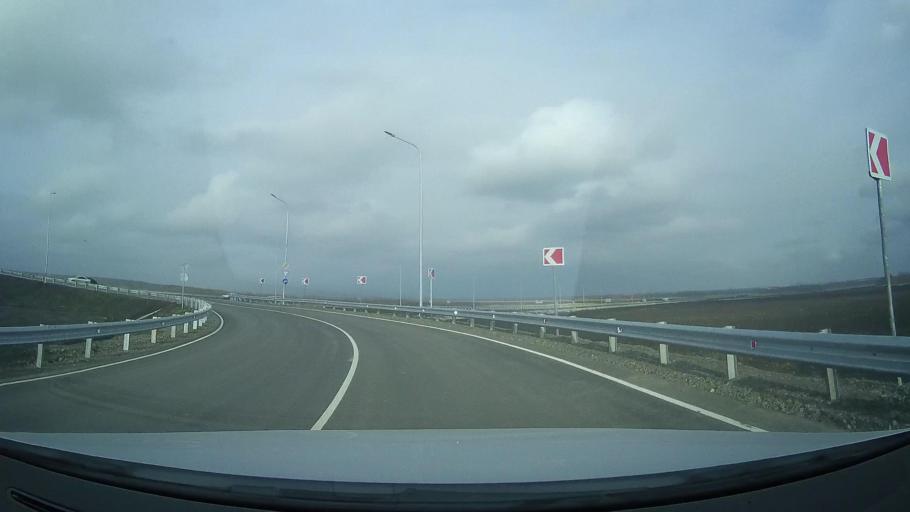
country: RU
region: Rostov
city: Grushevskaya
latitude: 47.4565
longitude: 39.8859
